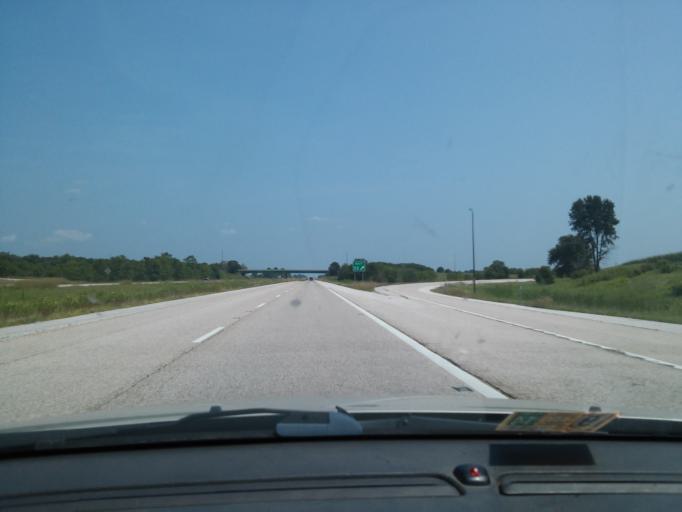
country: US
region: Illinois
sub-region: Scott County
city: Winchester
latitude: 39.6810
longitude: -90.4620
